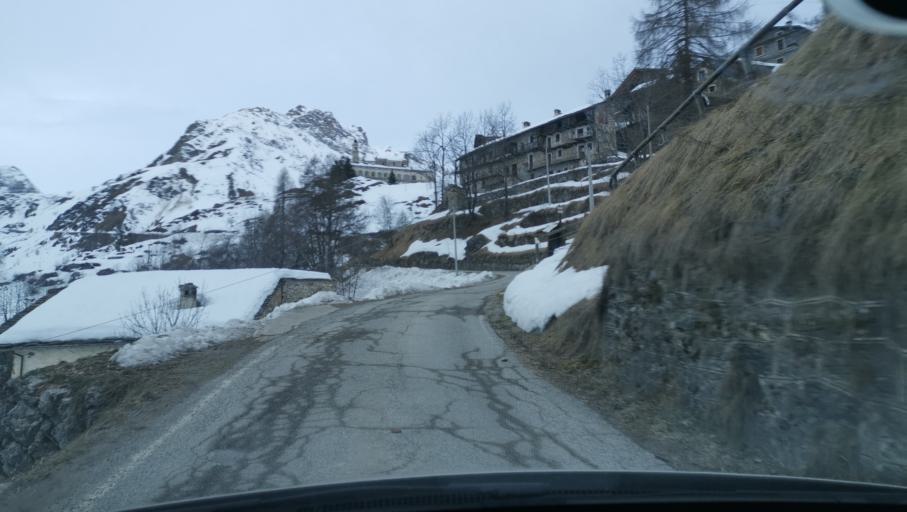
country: IT
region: Piedmont
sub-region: Provincia di Cuneo
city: Campomolino
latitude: 44.3995
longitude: 7.1761
